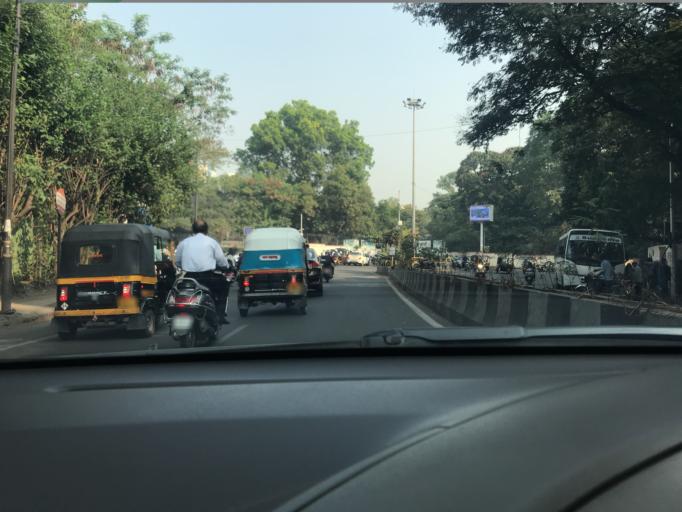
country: IN
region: Maharashtra
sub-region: Pune Division
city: Shivaji Nagar
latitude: 18.5194
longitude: 73.8304
